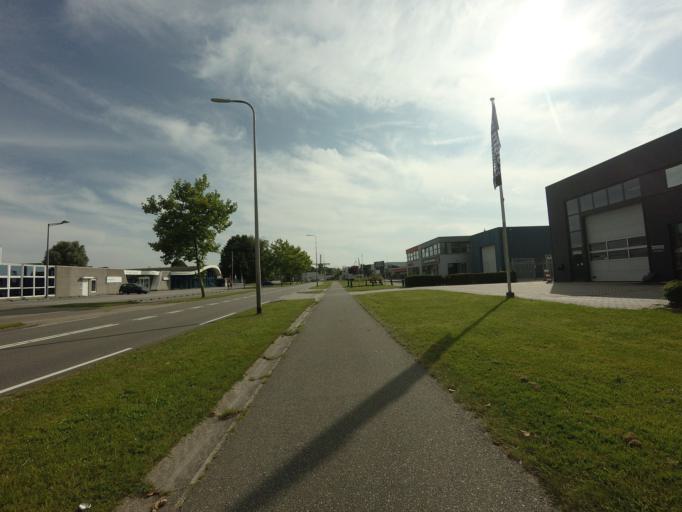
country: NL
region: Drenthe
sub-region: Gemeente Coevorden
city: Coevorden
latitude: 52.6625
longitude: 6.7253
